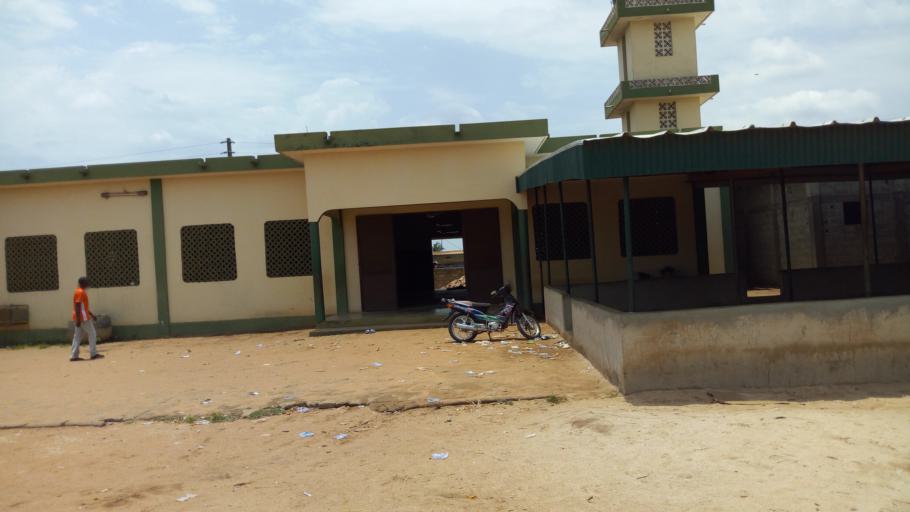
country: CI
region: Vallee du Bandama
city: Bouake
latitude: 7.7038
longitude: -5.0498
